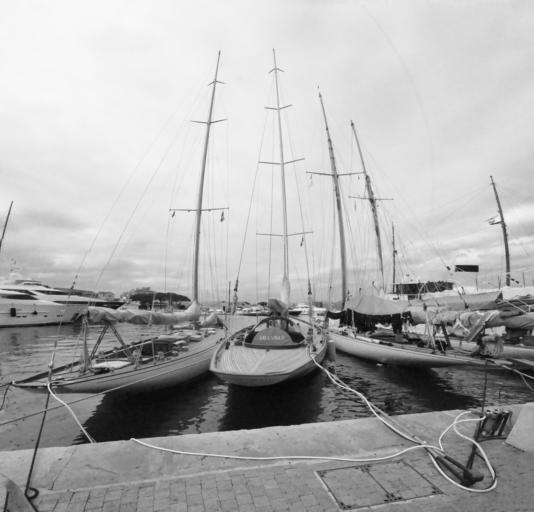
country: FR
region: Provence-Alpes-Cote d'Azur
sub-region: Departement du Var
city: Saint-Tropez
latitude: 43.2721
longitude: 6.6390
